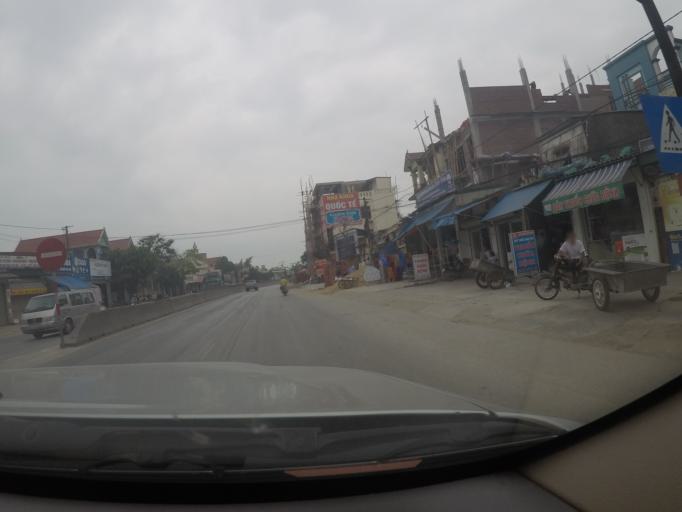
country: VN
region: Nghe An
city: Dien Chau
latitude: 19.0105
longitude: 105.5878
